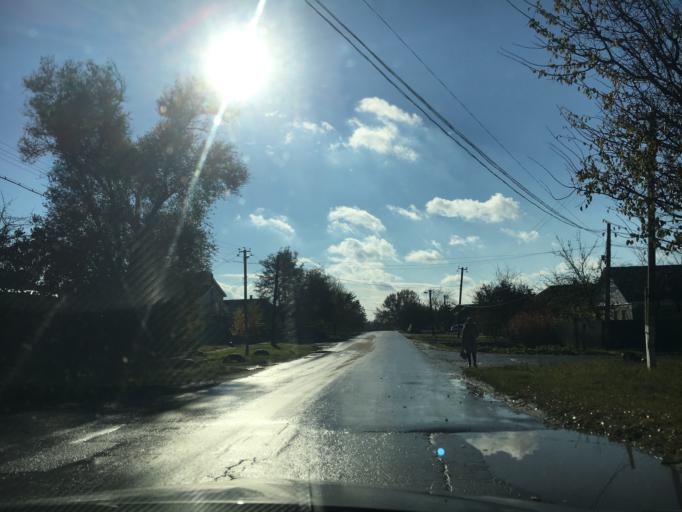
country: RU
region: Rostov
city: Matveyev Kurgan
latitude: 47.5745
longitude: 38.8682
